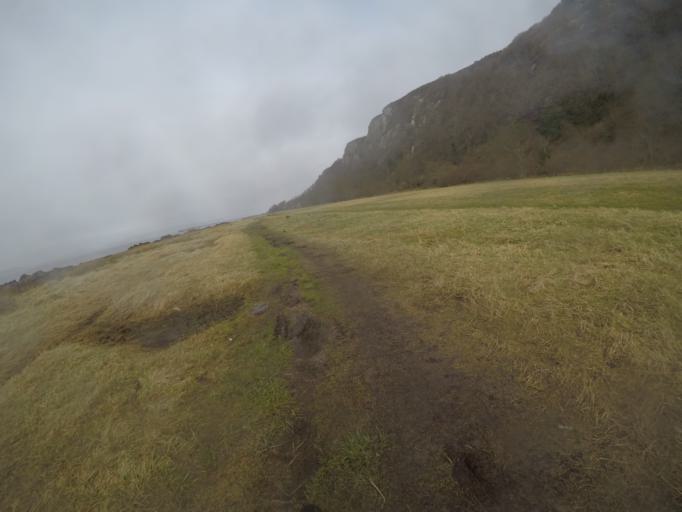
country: GB
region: Scotland
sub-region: North Ayrshire
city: Millport
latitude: 55.7086
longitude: -4.9041
